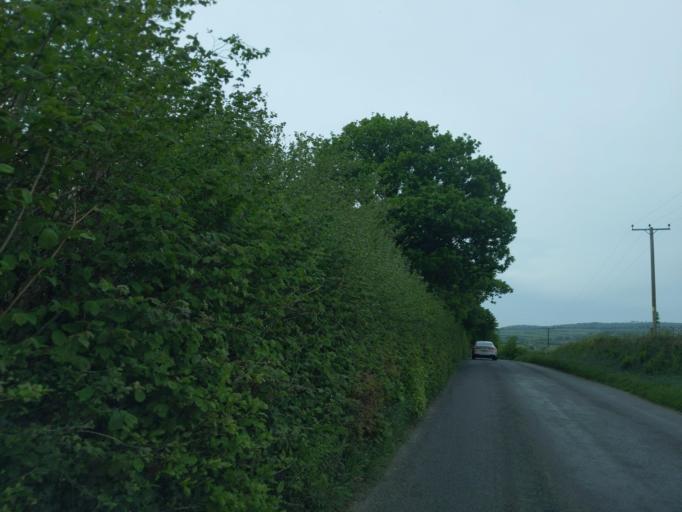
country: GB
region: England
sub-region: Devon
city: Plympton
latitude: 50.4203
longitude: -4.0467
